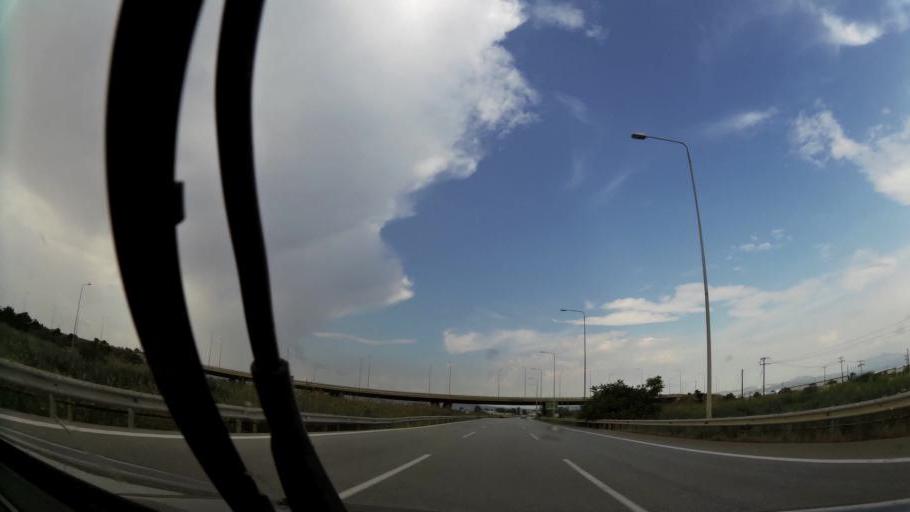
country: GR
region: Central Macedonia
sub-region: Nomos Thessalonikis
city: Sindos
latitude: 40.6485
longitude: 22.8114
